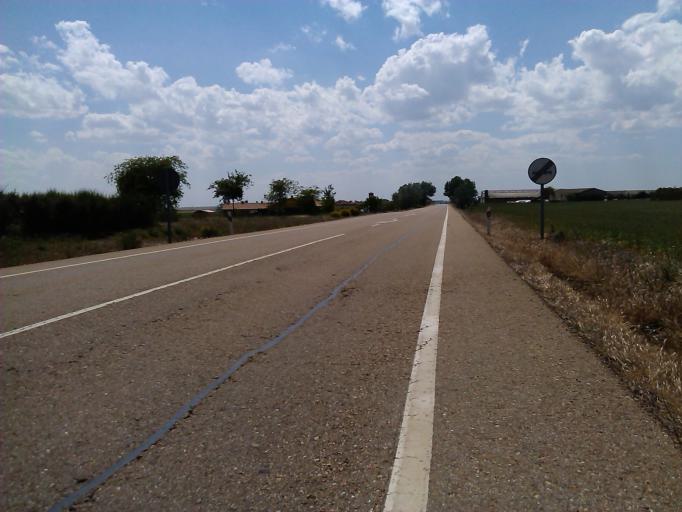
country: ES
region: Castille and Leon
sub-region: Provincia de Palencia
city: Ledigos
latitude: 42.3654
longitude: -4.8818
